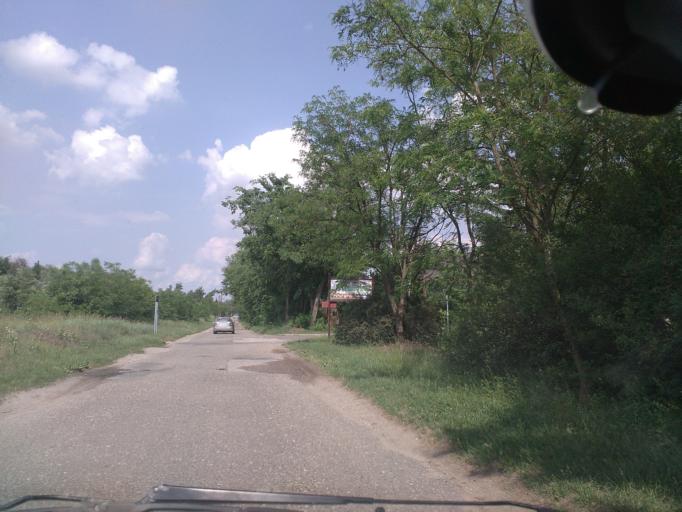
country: HU
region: Pest
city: Veresegyhaz
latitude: 47.6441
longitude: 19.2691
